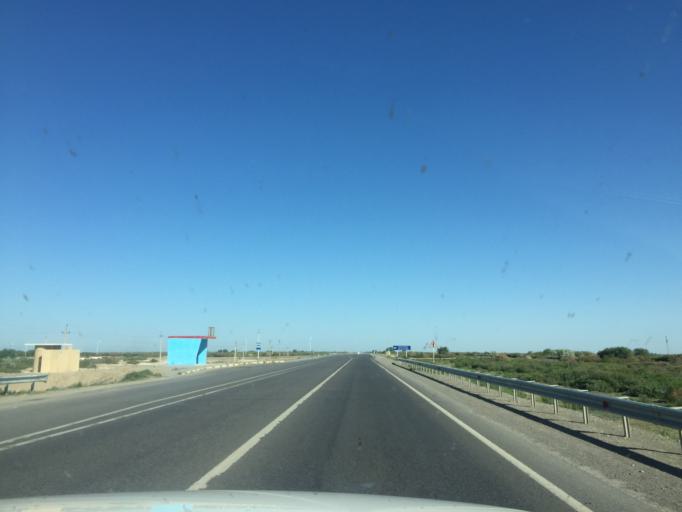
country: KZ
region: Qyzylorda
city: Kyzyl-Orda
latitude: 44.8592
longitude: 65.3717
